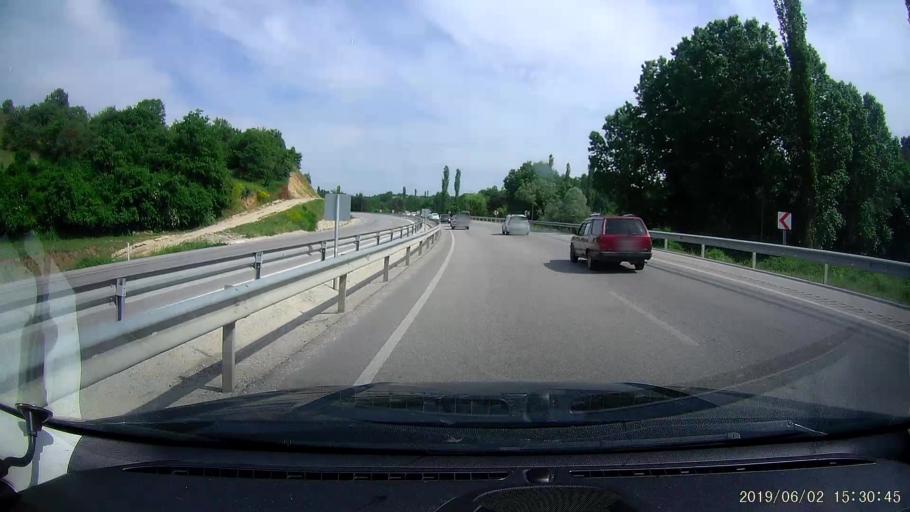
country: TR
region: Amasya
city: Saraycik
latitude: 40.9501
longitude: 35.1146
